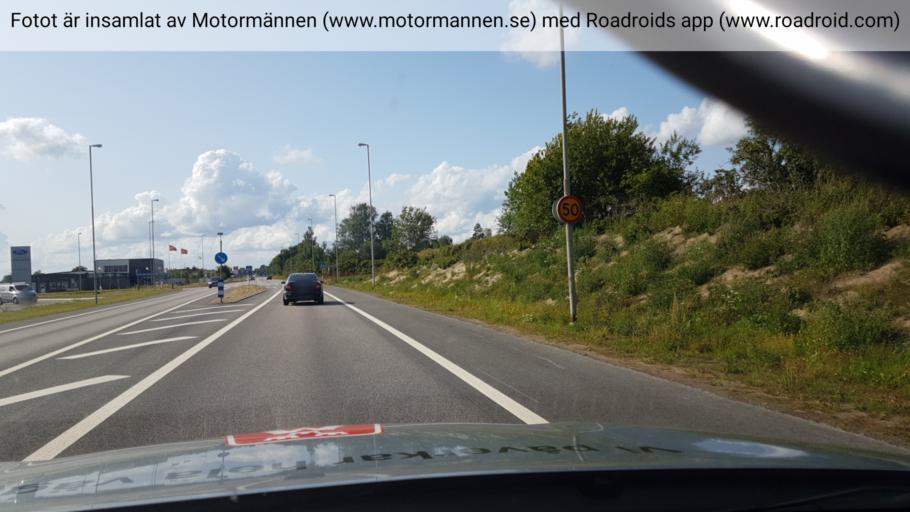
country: SE
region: Skane
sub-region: Hassleholms Kommun
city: Hassleholm
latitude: 56.1475
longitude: 13.7891
